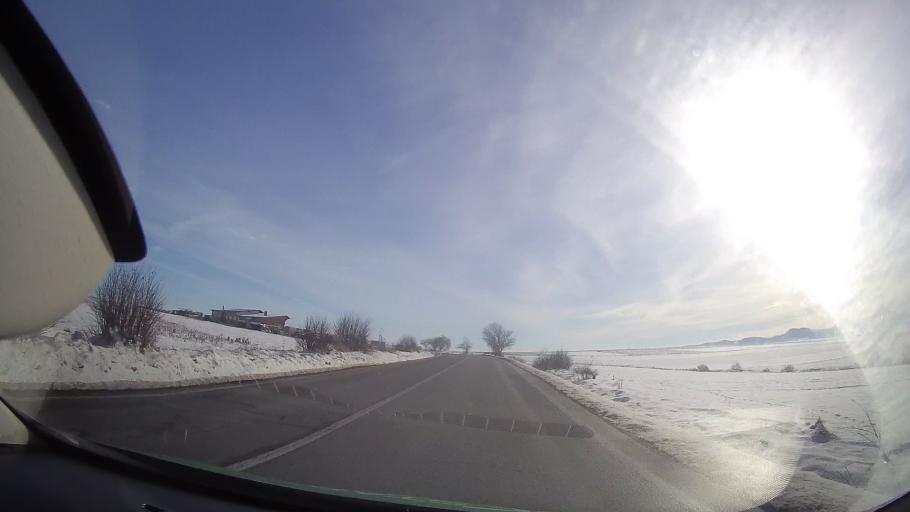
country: RO
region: Neamt
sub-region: Comuna Baltatesti
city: Valea Seaca
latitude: 47.1596
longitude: 26.3197
